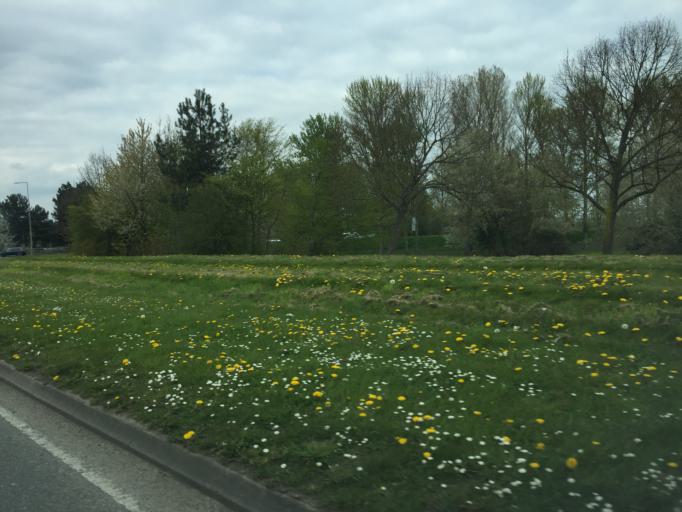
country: GB
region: England
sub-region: Milton Keynes
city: Broughton
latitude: 52.0459
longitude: -0.7232
